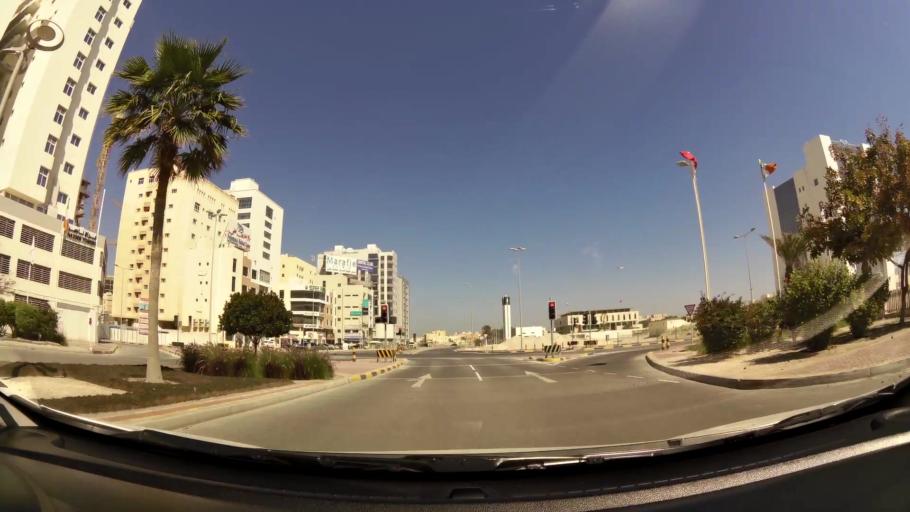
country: BH
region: Muharraq
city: Al Muharraq
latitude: 26.2636
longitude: 50.5982
